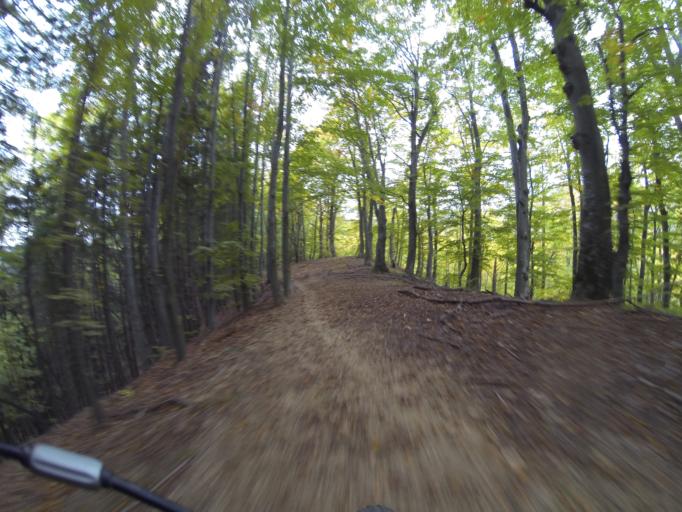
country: RO
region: Gorj
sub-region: Comuna Tismana
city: Sohodol
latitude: 45.0878
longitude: 22.8850
